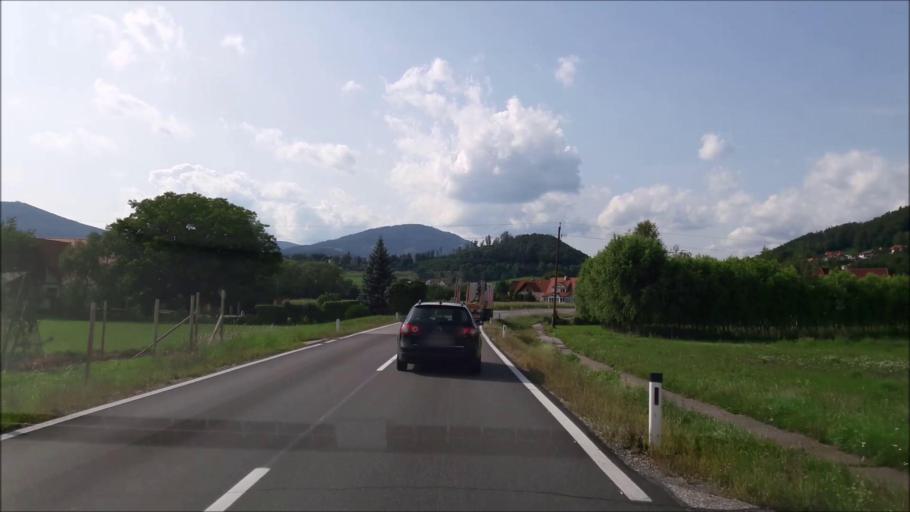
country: AT
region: Styria
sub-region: Politischer Bezirk Weiz
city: Floing
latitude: 47.2449
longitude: 15.7335
